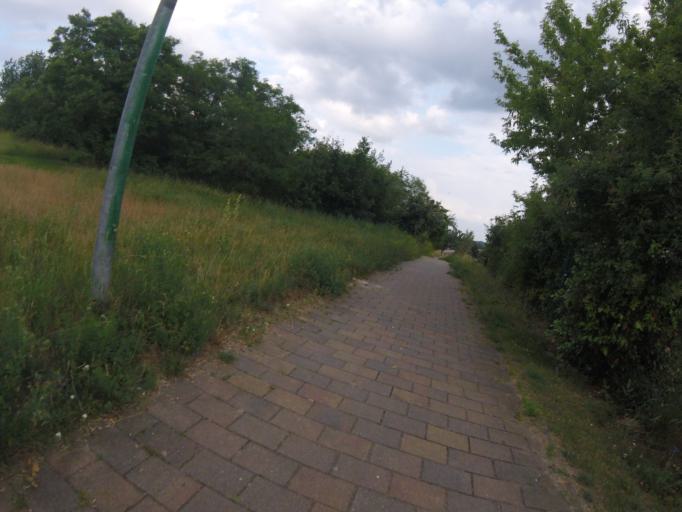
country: DE
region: Brandenburg
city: Konigs Wusterhausen
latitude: 52.2971
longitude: 13.5885
